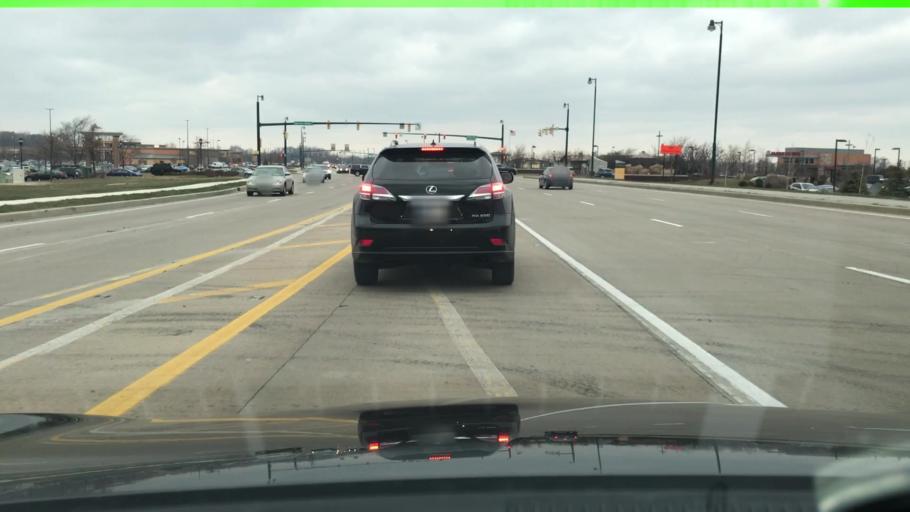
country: US
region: Indiana
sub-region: Hancock County
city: McCordsville
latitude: 39.9931
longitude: -85.9272
